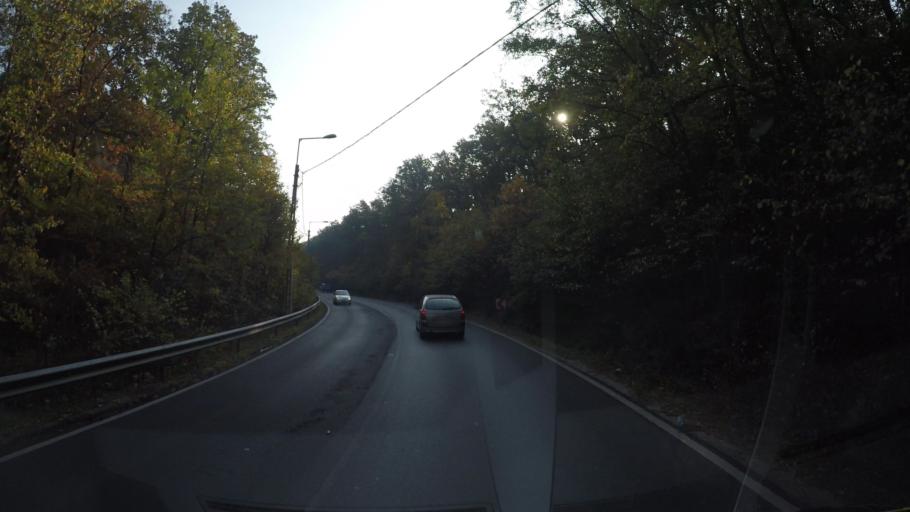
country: HU
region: Pest
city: Budaors
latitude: 47.4417
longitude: 18.9971
